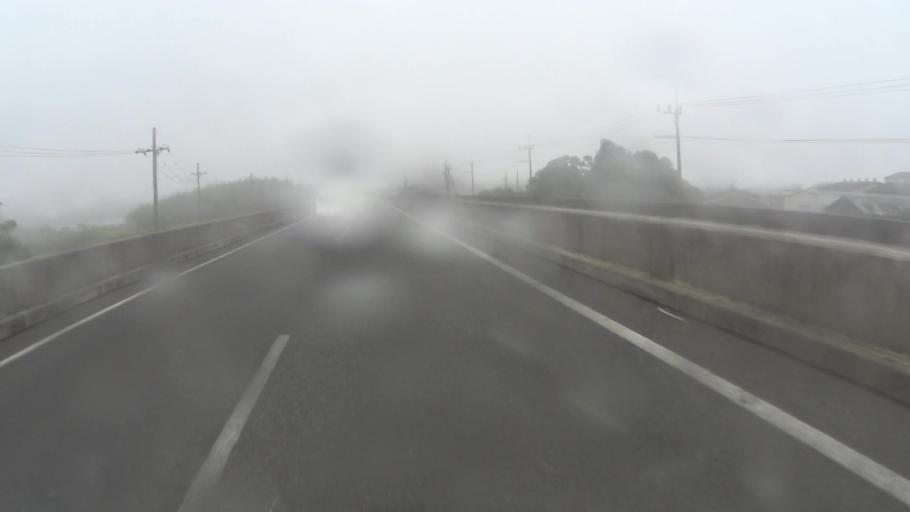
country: JP
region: Kyoto
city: Kameoka
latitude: 35.0201
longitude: 135.5522
